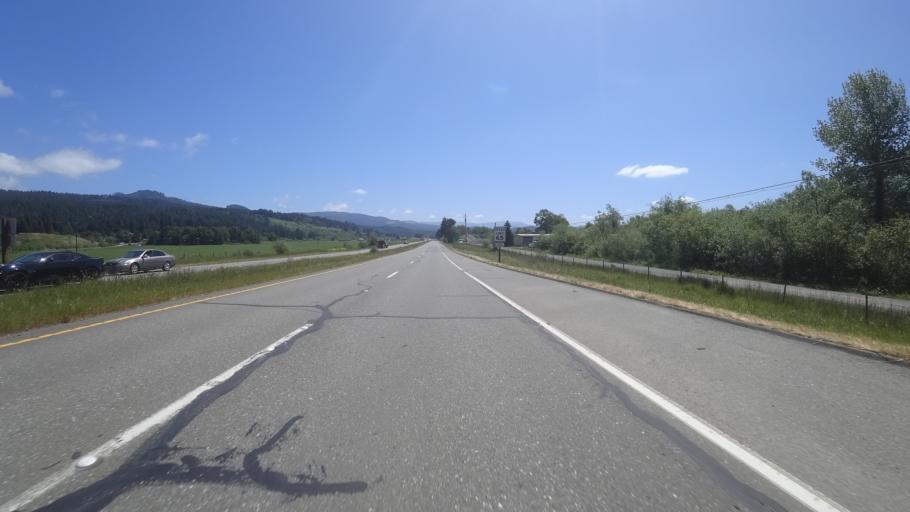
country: US
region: California
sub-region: Humboldt County
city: Blue Lake
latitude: 40.8966
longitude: -124.0180
